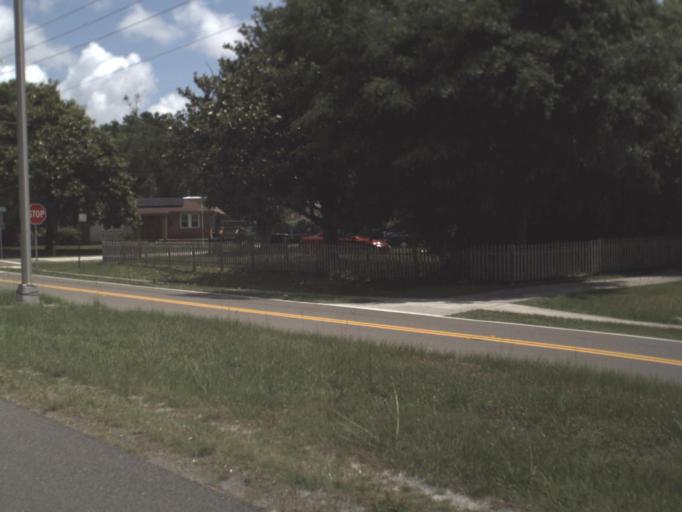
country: US
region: Florida
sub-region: Duval County
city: Jacksonville
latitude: 30.2915
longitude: -81.5590
